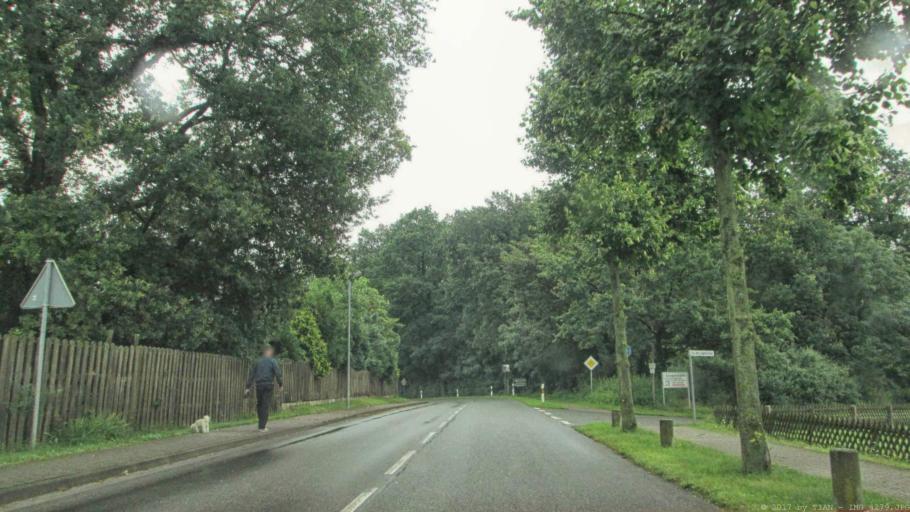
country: DE
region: Lower Saxony
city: Danndorf
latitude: 52.4269
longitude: 10.9241
